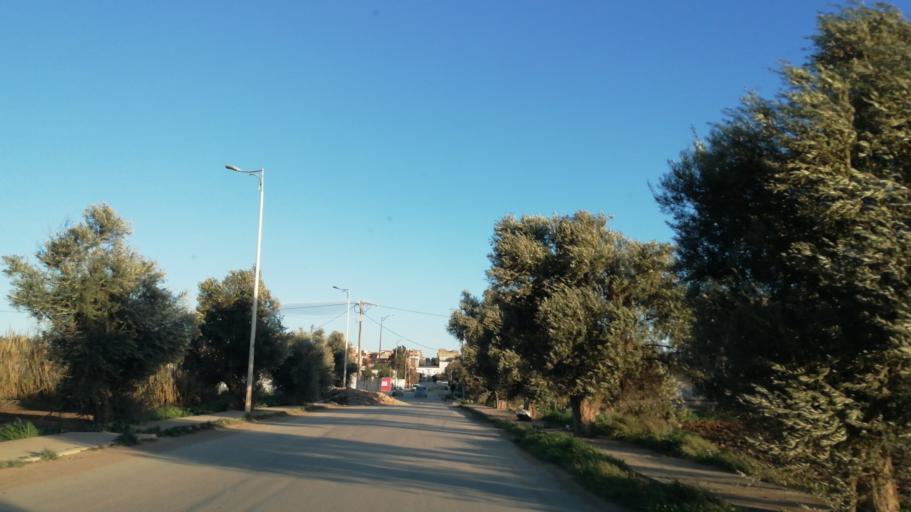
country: DZ
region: Oran
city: Sidi ech Chahmi
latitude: 35.6935
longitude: -0.5070
